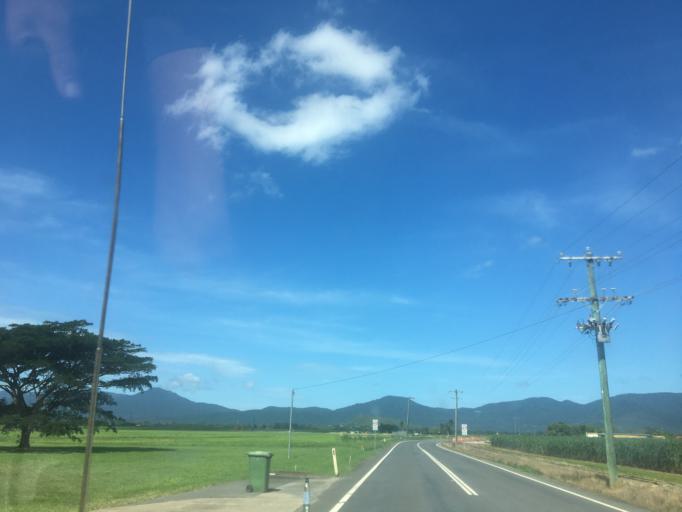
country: AU
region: Queensland
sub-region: Cairns
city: Woree
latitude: -17.0608
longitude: 145.7641
